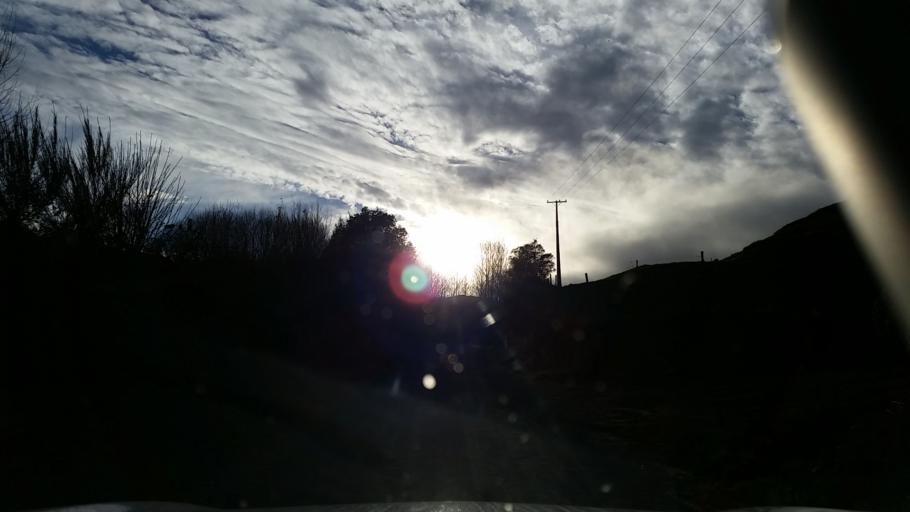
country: NZ
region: Bay of Plenty
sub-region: Rotorua District
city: Rotorua
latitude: -38.2987
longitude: 176.2763
